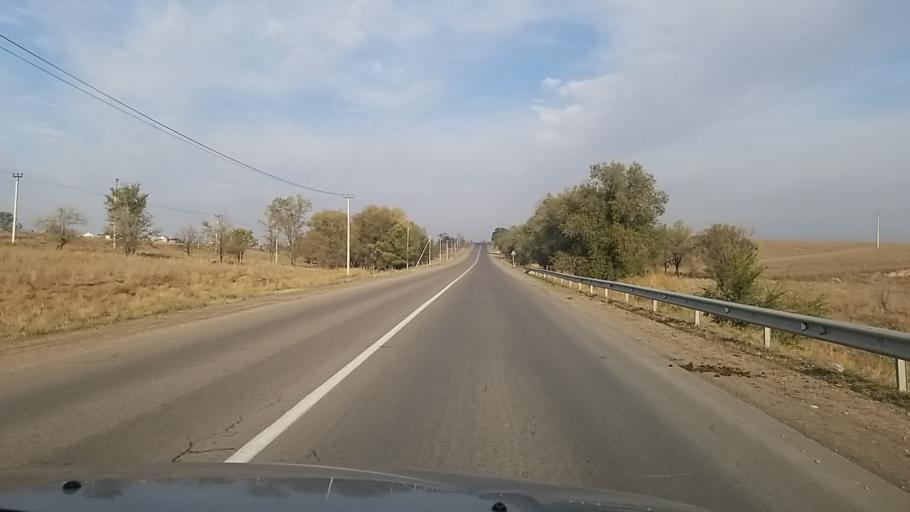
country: KZ
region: Almaty Oblysy
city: Burunday
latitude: 43.4706
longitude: 76.6984
